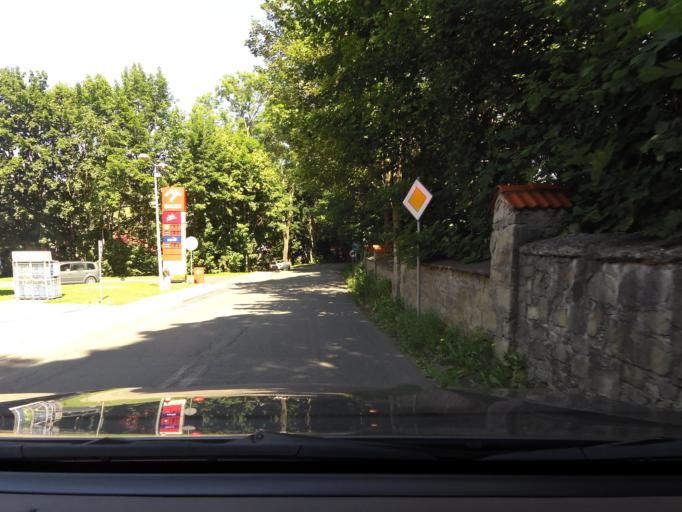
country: PL
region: Silesian Voivodeship
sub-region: Powiat zywiecki
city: Rajcza
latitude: 49.4996
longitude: 19.1009
